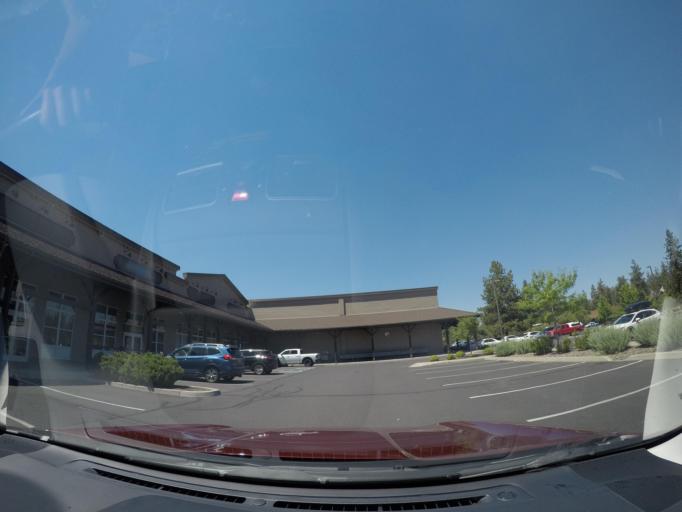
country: US
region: Oregon
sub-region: Deschutes County
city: Sisters
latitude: 44.2961
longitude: -121.5619
